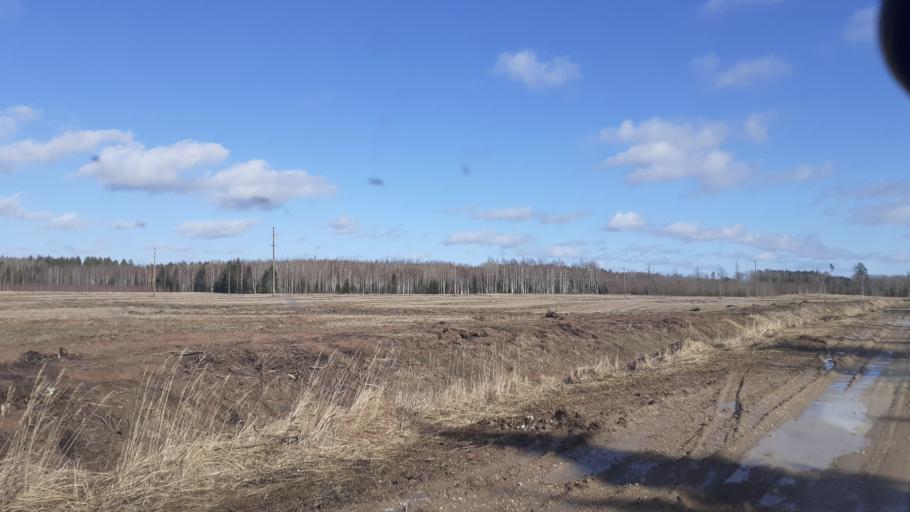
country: LV
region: Kuldigas Rajons
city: Kuldiga
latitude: 56.9335
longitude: 22.1772
